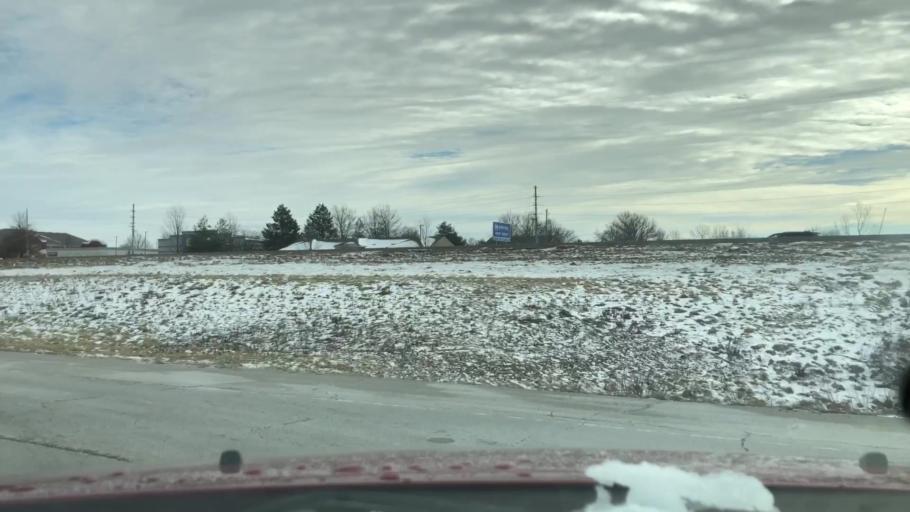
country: US
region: Missouri
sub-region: Jackson County
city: Lees Summit
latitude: 38.9039
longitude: -94.3556
